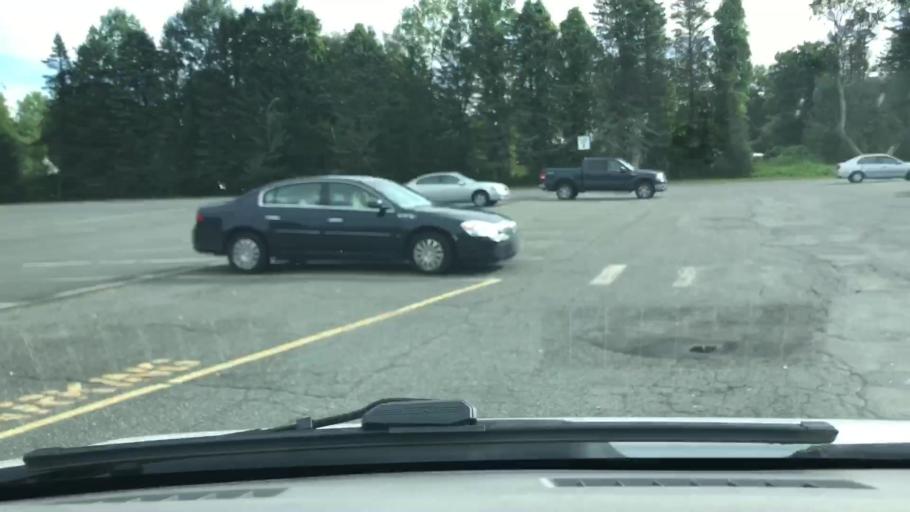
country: US
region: Massachusetts
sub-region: Franklin County
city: South Deerfield
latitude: 42.4889
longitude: -72.6077
